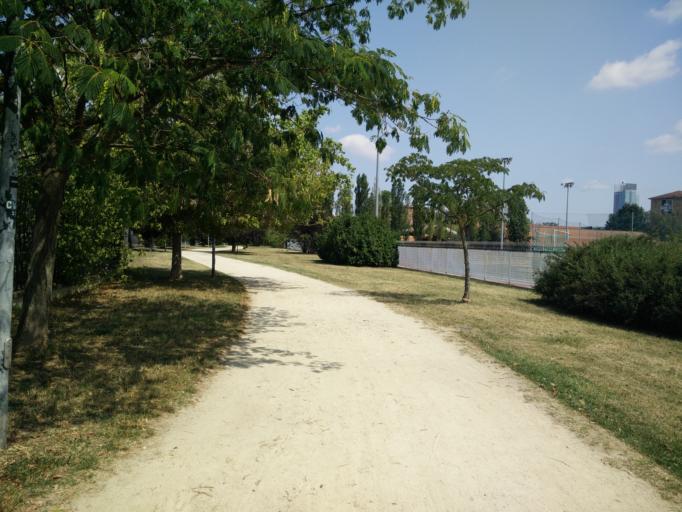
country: IT
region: Piedmont
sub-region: Provincia di Torino
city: Nichelino
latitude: 45.0154
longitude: 7.6447
